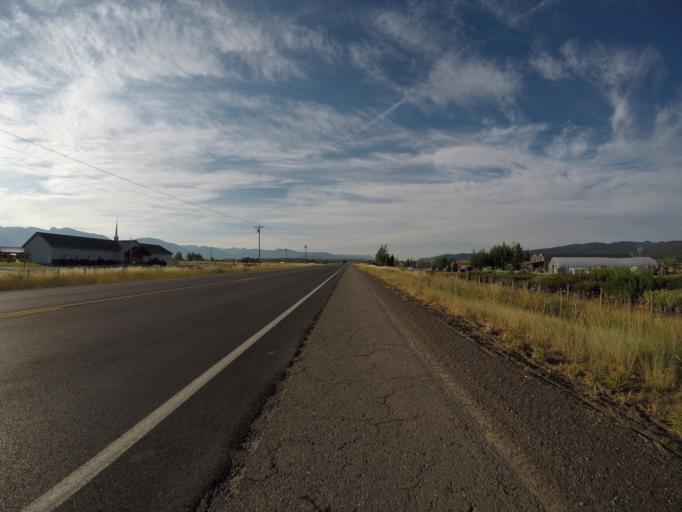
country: US
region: Wyoming
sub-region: Lincoln County
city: Afton
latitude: 42.9510
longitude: -111.0114
